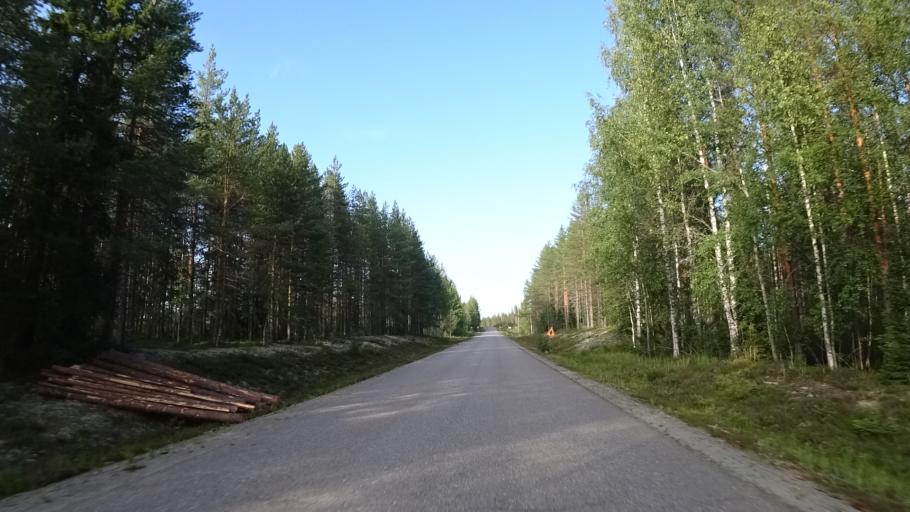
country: FI
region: North Karelia
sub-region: Joensuu
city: Eno
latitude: 63.0632
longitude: 30.5522
